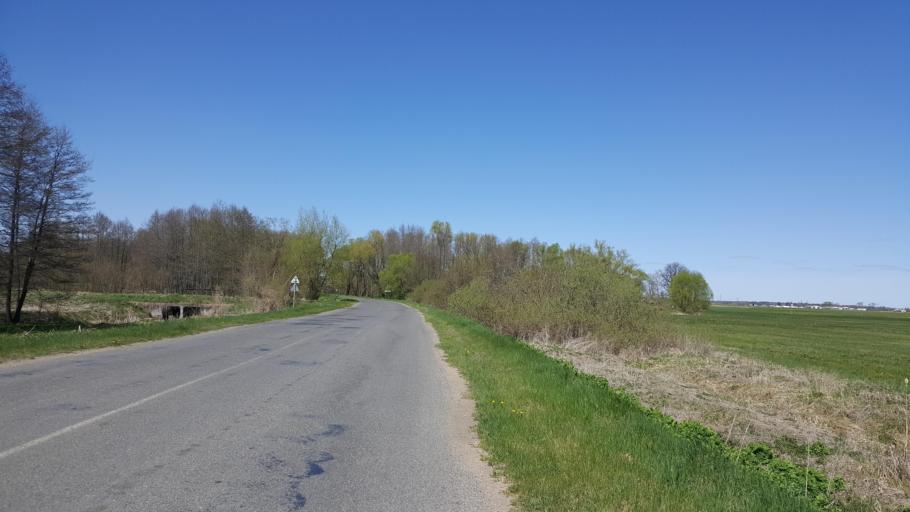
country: BY
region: Brest
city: Charnawchytsy
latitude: 52.3222
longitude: 23.6145
